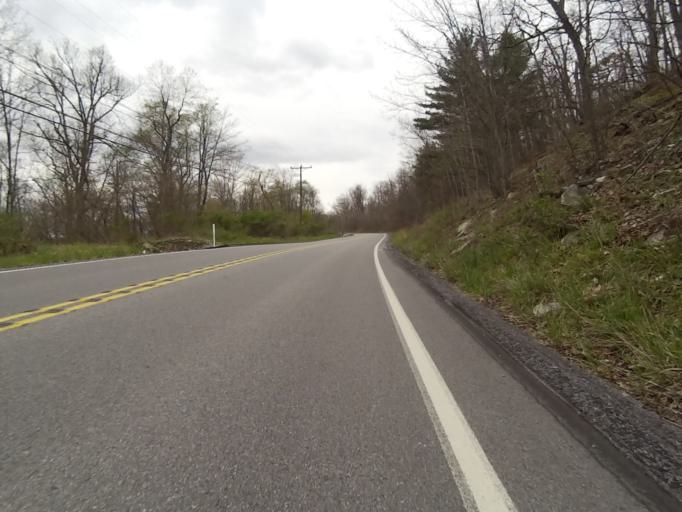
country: US
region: Pennsylvania
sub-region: Clearfield County
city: Troy
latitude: 40.9006
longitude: -78.1552
